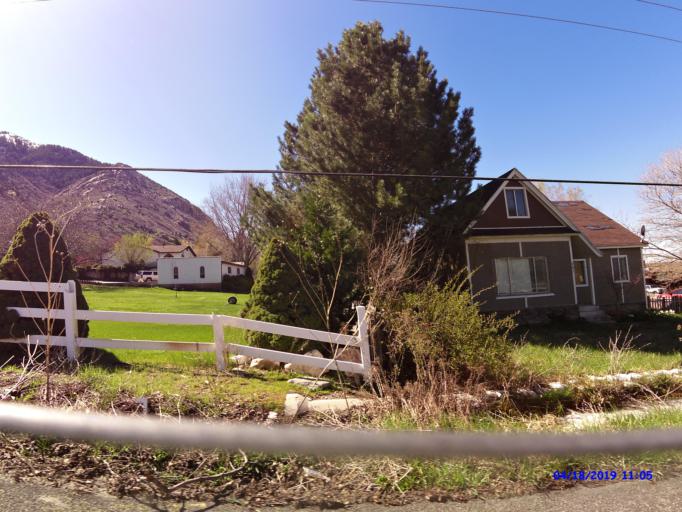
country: US
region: Utah
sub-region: Weber County
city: North Ogden
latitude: 41.2889
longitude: -111.9489
